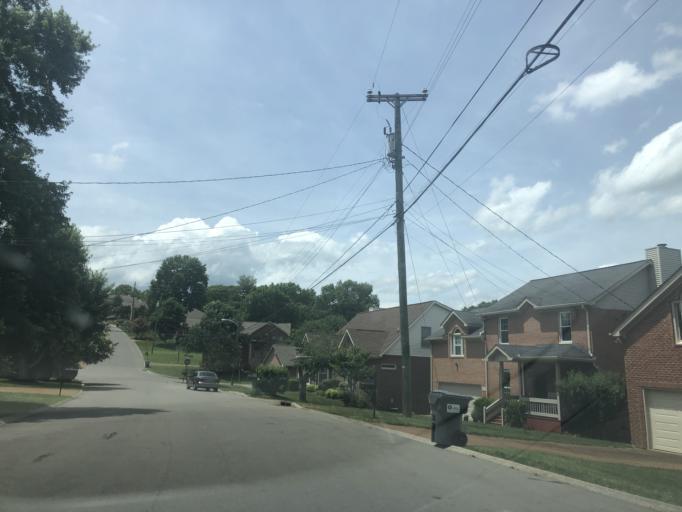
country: US
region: Tennessee
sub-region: Cheatham County
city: Pegram
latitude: 36.0502
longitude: -86.9592
